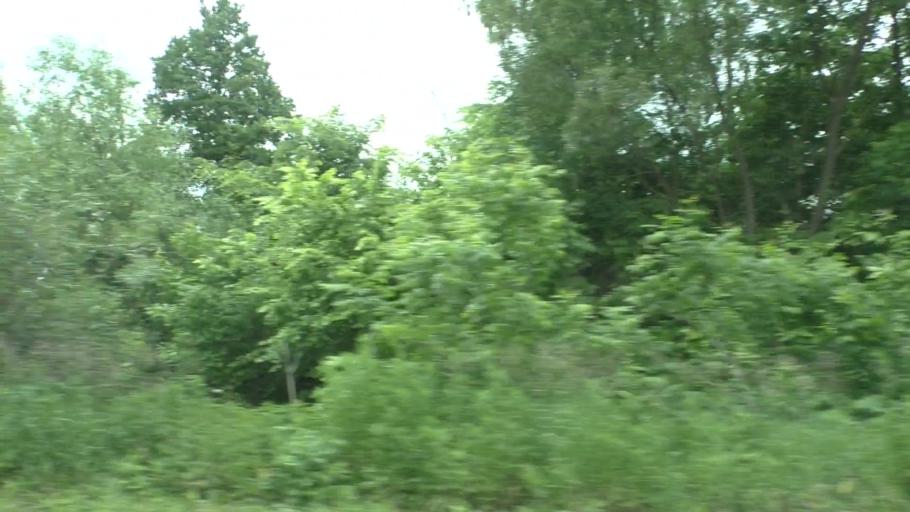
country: RU
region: Moskovskaya
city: Yegor'yevsk
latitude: 55.4016
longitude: 39.0036
